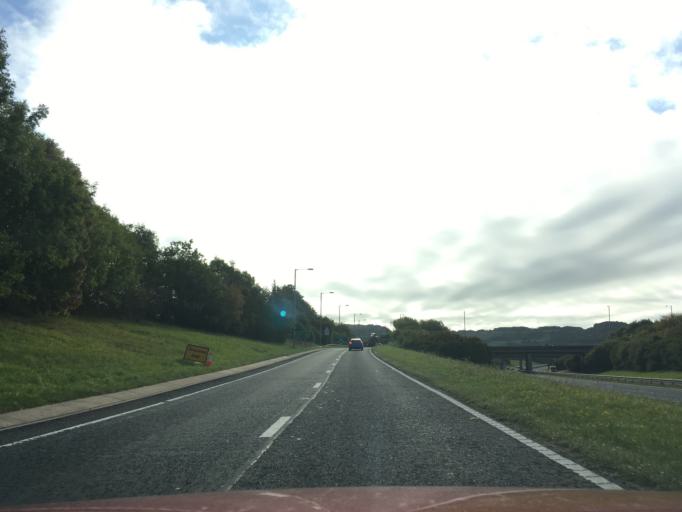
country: GB
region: England
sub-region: Gloucestershire
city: Shurdington
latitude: 51.8508
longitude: -2.1423
